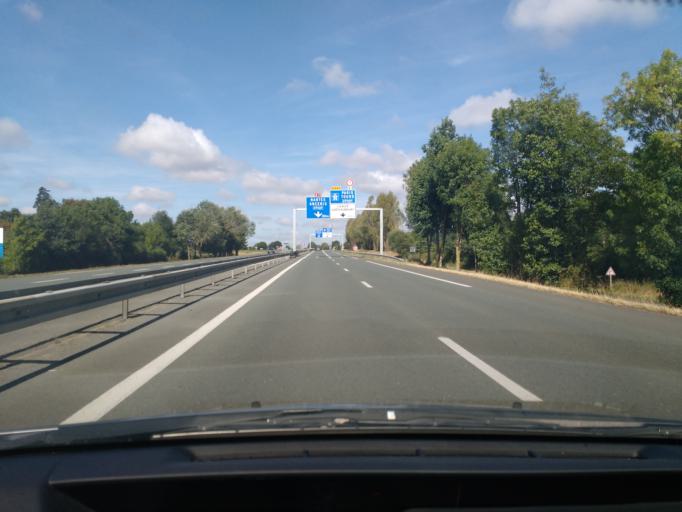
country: FR
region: Pays de la Loire
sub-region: Departement de Maine-et-Loire
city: Saint-Lambert-la-Potherie
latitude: 47.4664
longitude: -0.6724
